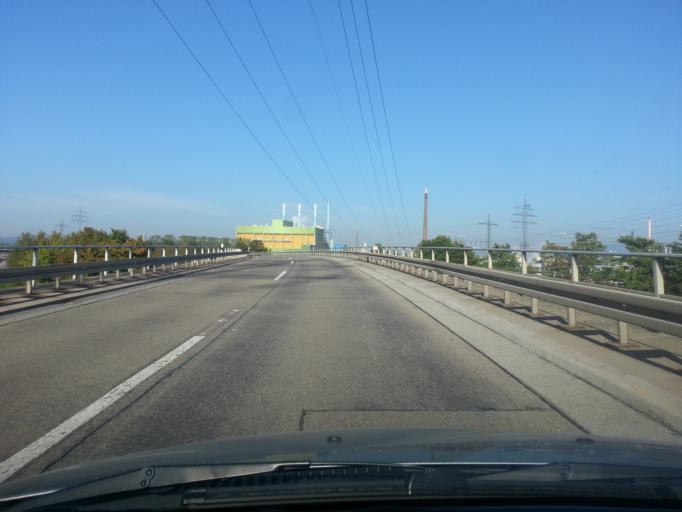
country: DE
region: Hesse
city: Kelsterbach
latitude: 50.0761
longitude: 8.5402
